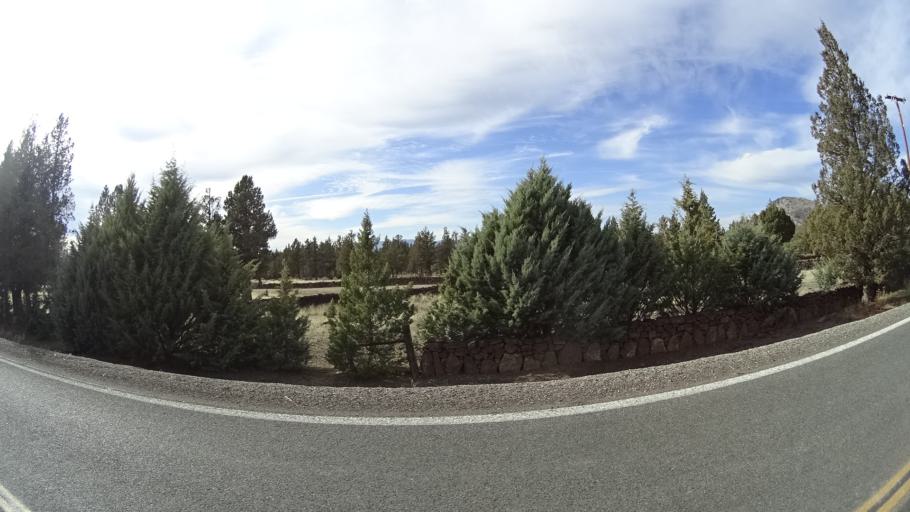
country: US
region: California
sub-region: Siskiyou County
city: Montague
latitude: 41.6487
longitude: -122.3993
